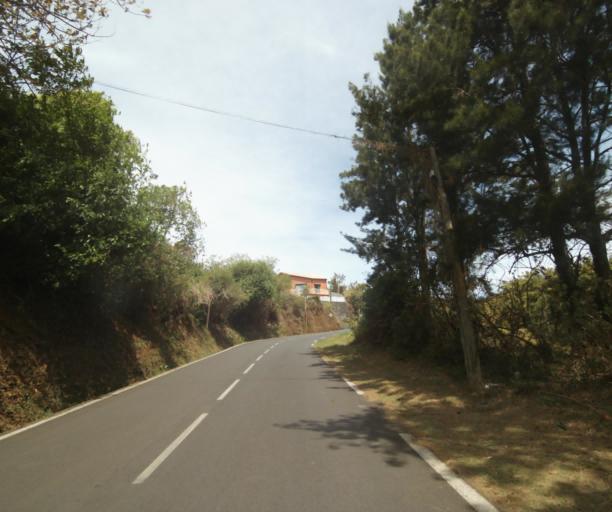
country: RE
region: Reunion
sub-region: Reunion
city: Saint-Paul
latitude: -21.0436
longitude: 55.3074
